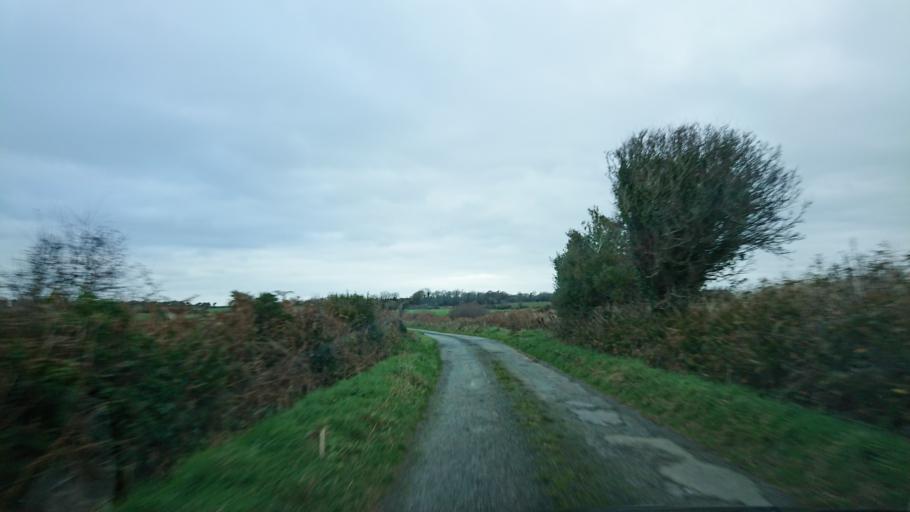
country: IE
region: Munster
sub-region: Waterford
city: Dunmore East
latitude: 52.1853
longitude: -7.0428
